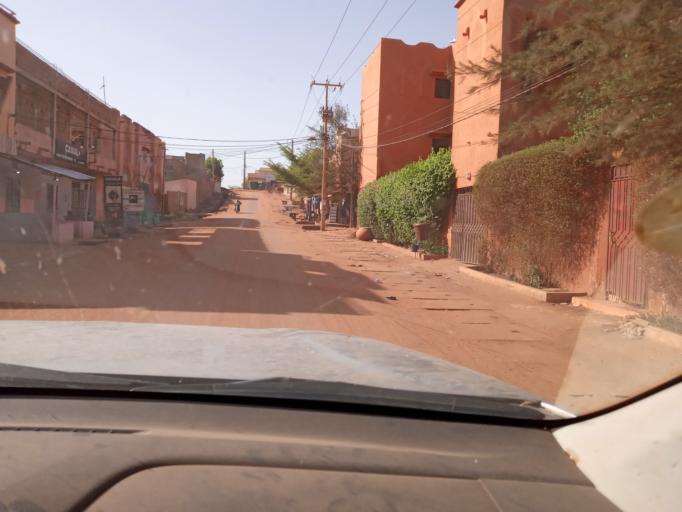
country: ML
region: Bamako
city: Bamako
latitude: 12.6722
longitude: -7.9179
